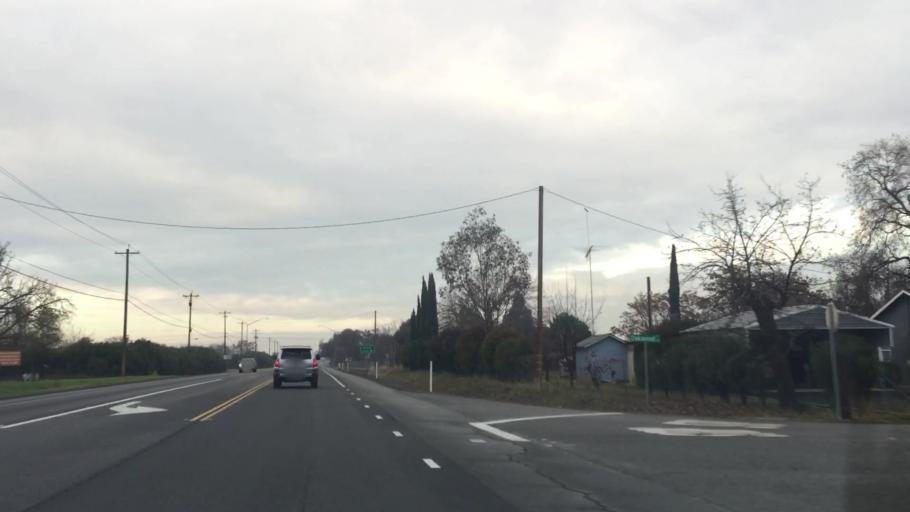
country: US
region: California
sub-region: Butte County
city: Palermo
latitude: 39.4272
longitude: -121.6051
